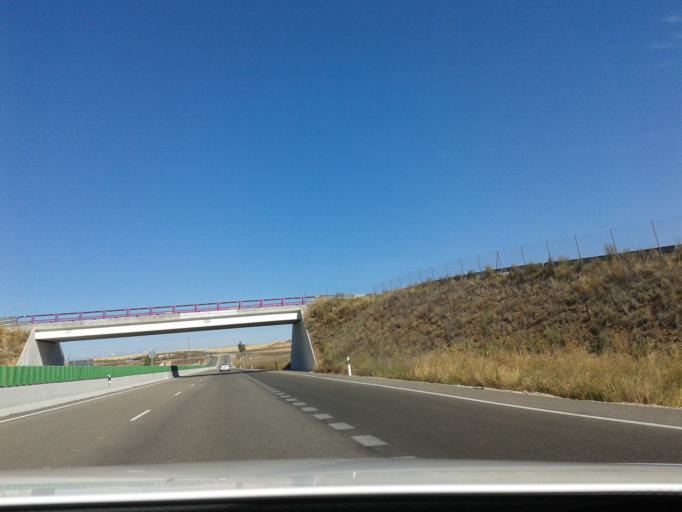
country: ES
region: Castille-La Mancha
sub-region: Provincia de Guadalajara
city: Azuqueca de Henares
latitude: 40.5820
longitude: -3.2638
